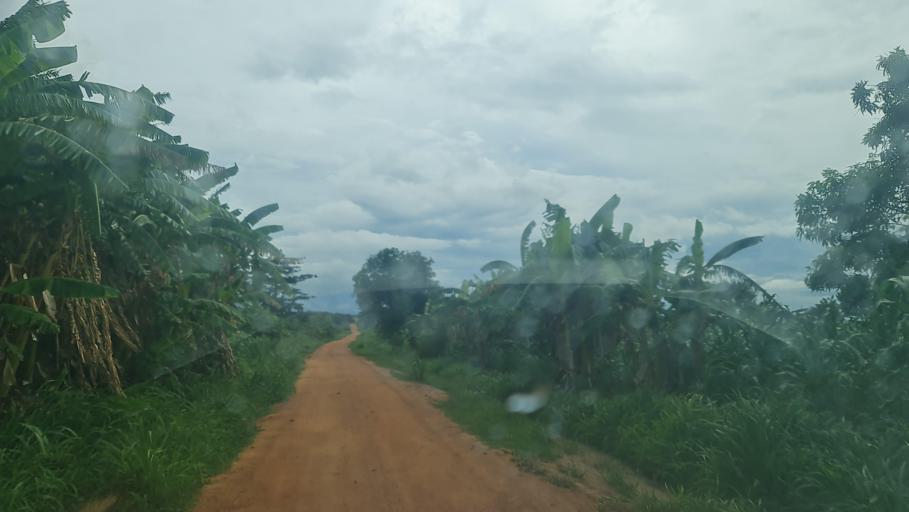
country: MW
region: Southern Region
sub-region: Nsanje District
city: Nsanje
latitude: -17.3956
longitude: 35.5782
